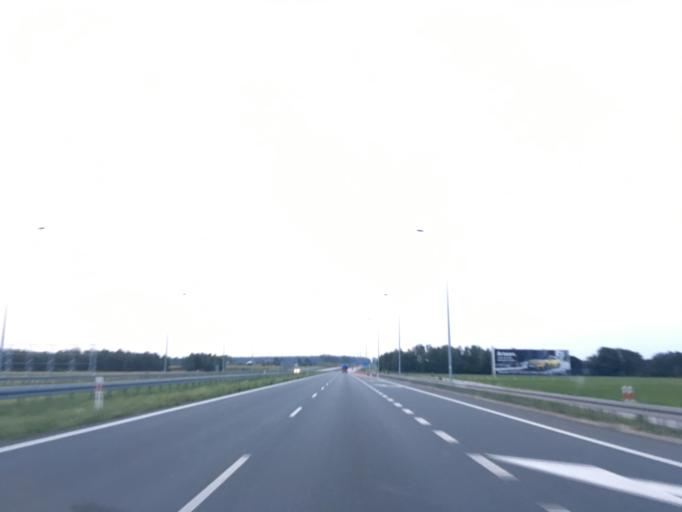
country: PL
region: Lodz Voivodeship
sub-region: Powiat zgierski
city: Strykow
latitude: 51.8786
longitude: 19.6467
